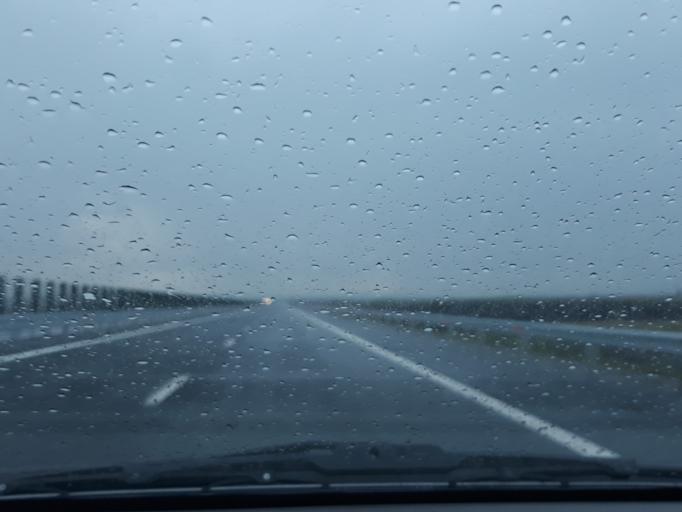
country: RO
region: Mures
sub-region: Comuna Ogra
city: Ogra
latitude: 46.4362
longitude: 24.3092
